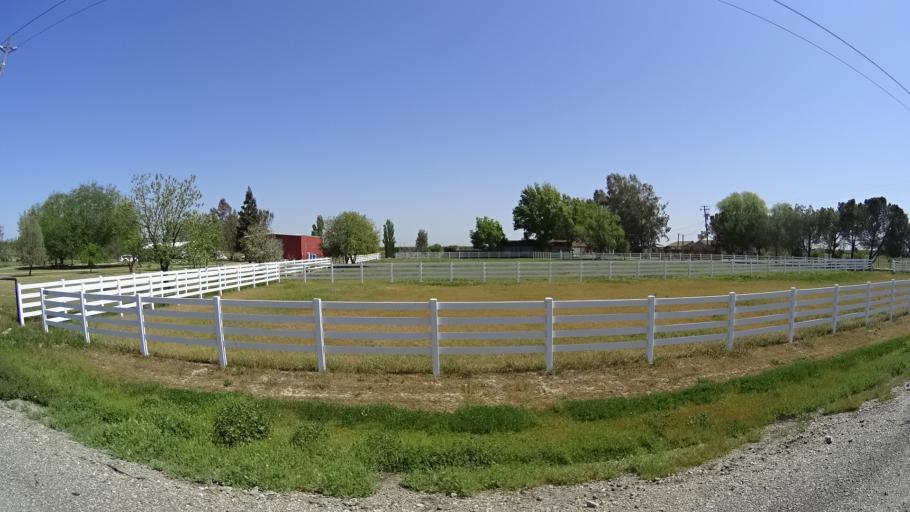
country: US
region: California
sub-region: Glenn County
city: Orland
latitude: 39.6382
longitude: -122.1973
